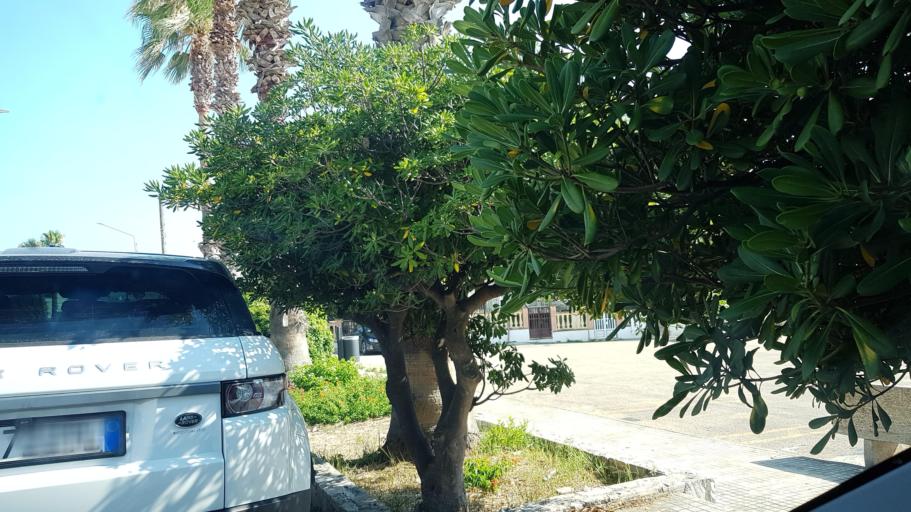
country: IT
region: Apulia
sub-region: Provincia di Lecce
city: Gemini
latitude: 39.8404
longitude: 18.2089
